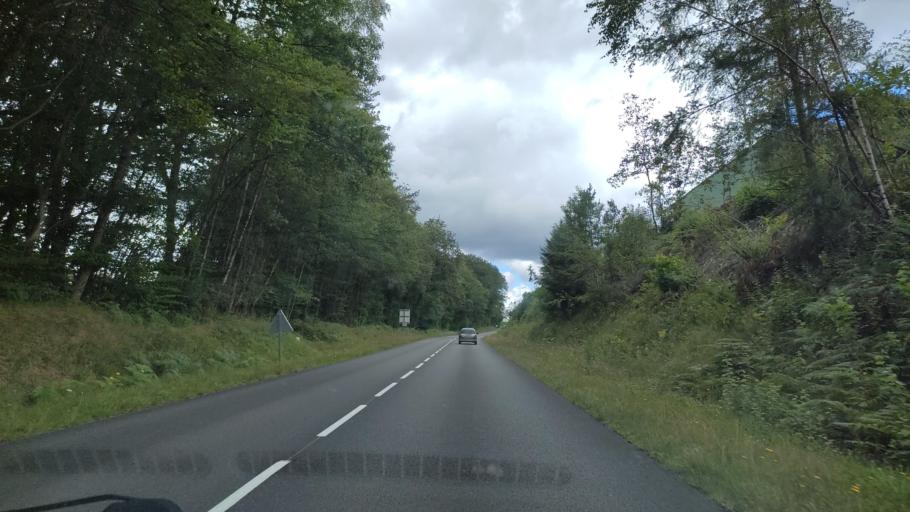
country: FR
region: Limousin
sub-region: Departement de la Haute-Vienne
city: Rilhac-Rancon
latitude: 45.9102
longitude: 1.3296
